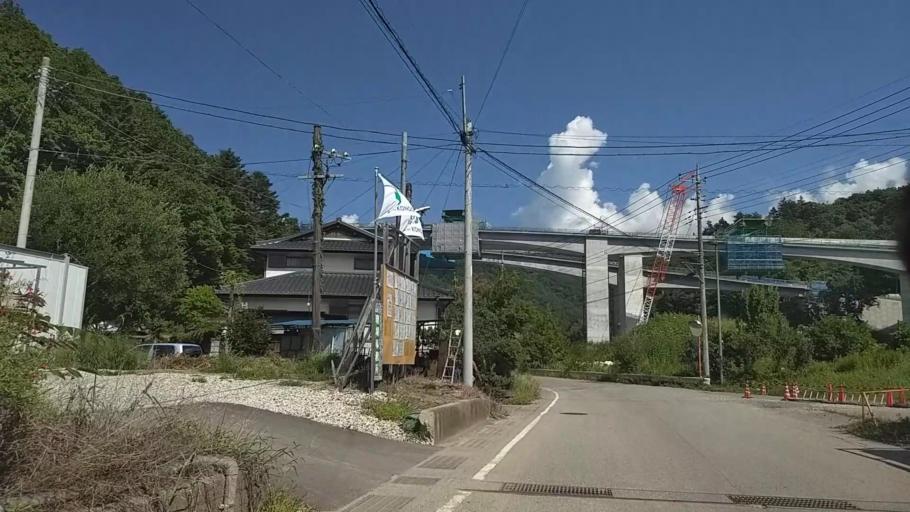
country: JP
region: Yamanashi
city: Ryuo
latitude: 35.4598
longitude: 138.4484
